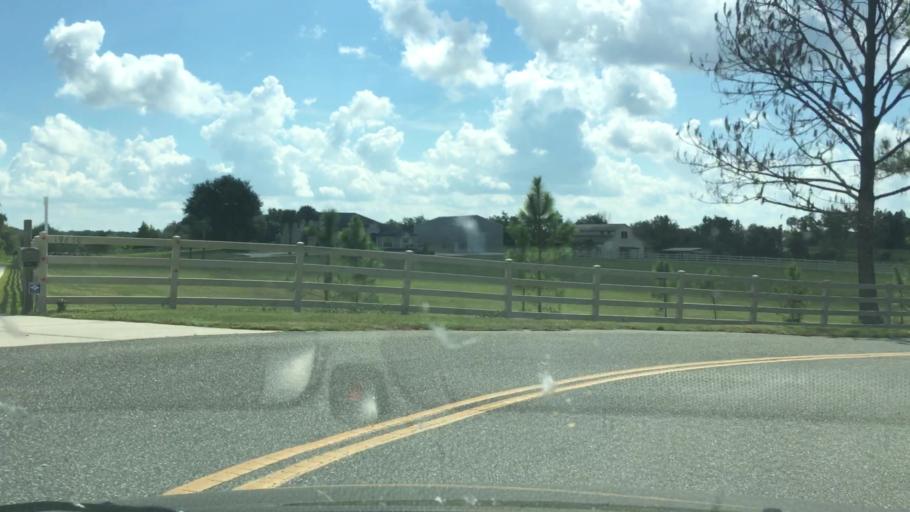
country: US
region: Florida
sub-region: Lake County
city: Montverde
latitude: 28.6373
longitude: -81.7146
